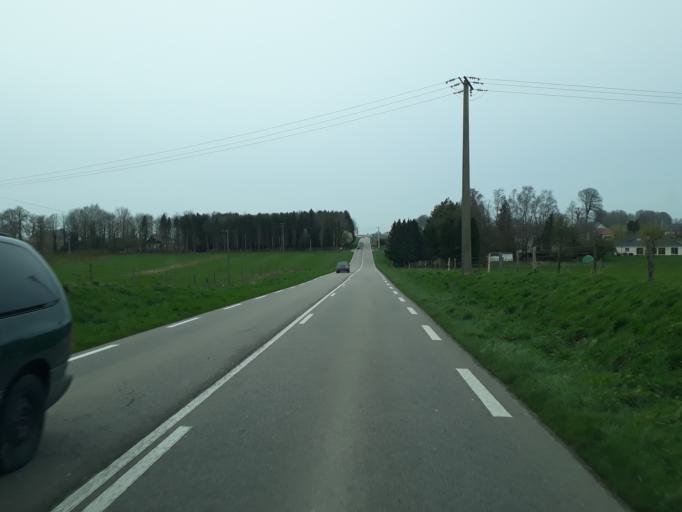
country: FR
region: Haute-Normandie
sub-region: Departement de la Seine-Maritime
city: Breaute
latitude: 49.6318
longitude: 0.3910
